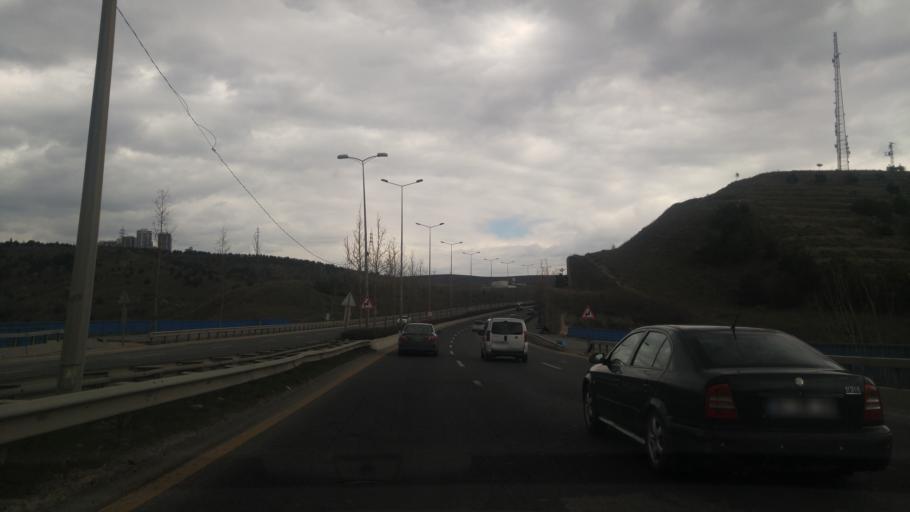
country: TR
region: Ankara
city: Mamak
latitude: 39.8885
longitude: 32.9106
